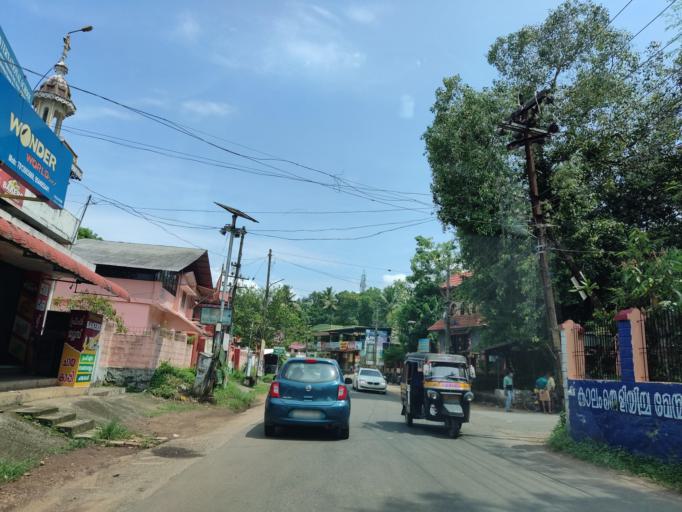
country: IN
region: Kerala
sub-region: Alappuzha
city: Chengannur
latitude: 9.3074
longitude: 76.5885
